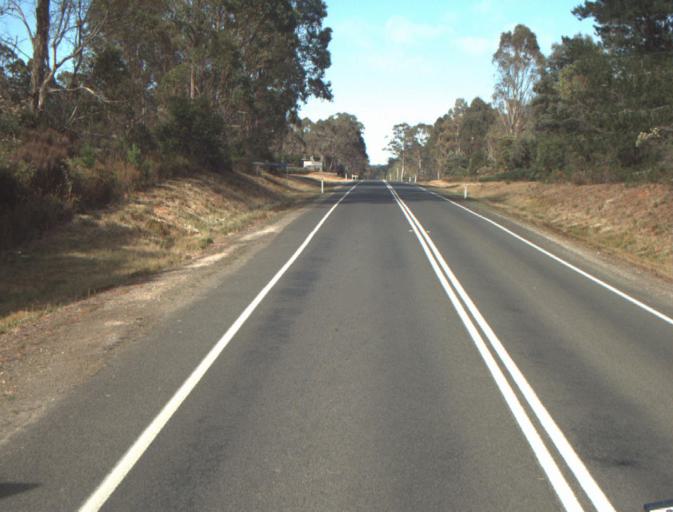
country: AU
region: Tasmania
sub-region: Launceston
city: Mayfield
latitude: -41.3104
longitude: 147.2012
